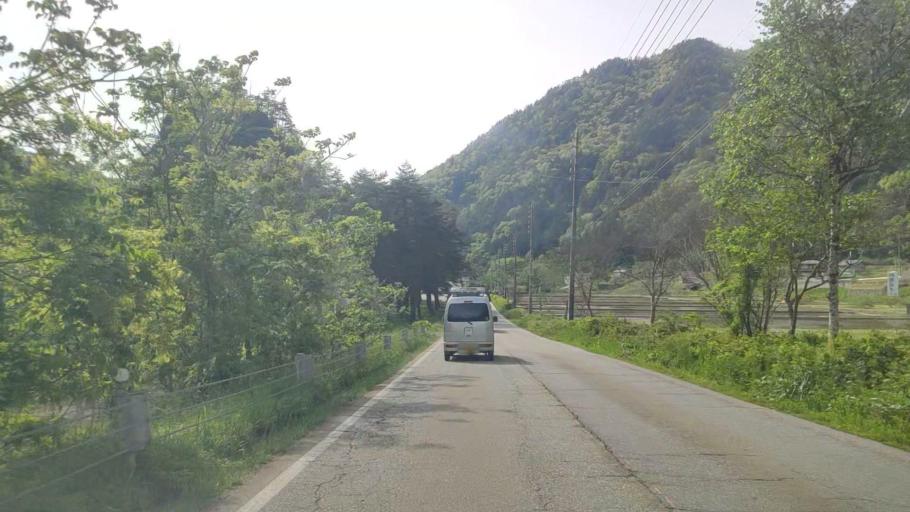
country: JP
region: Gifu
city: Takayama
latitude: 36.2672
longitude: 137.4240
